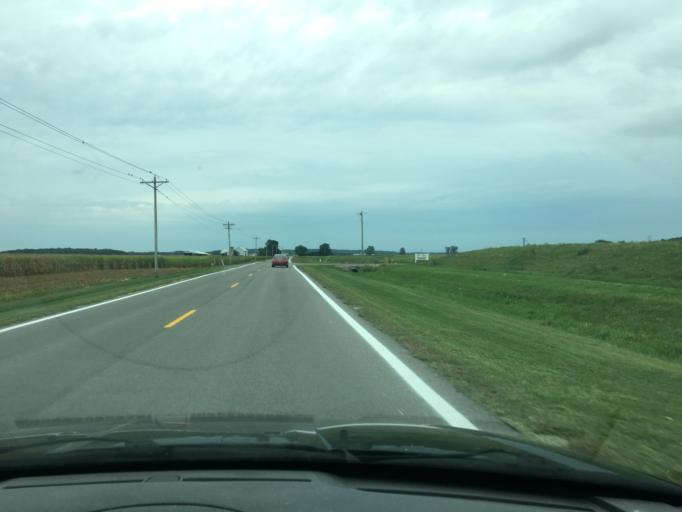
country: US
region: Ohio
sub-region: Logan County
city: West Liberty
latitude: 40.1853
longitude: -83.7820
